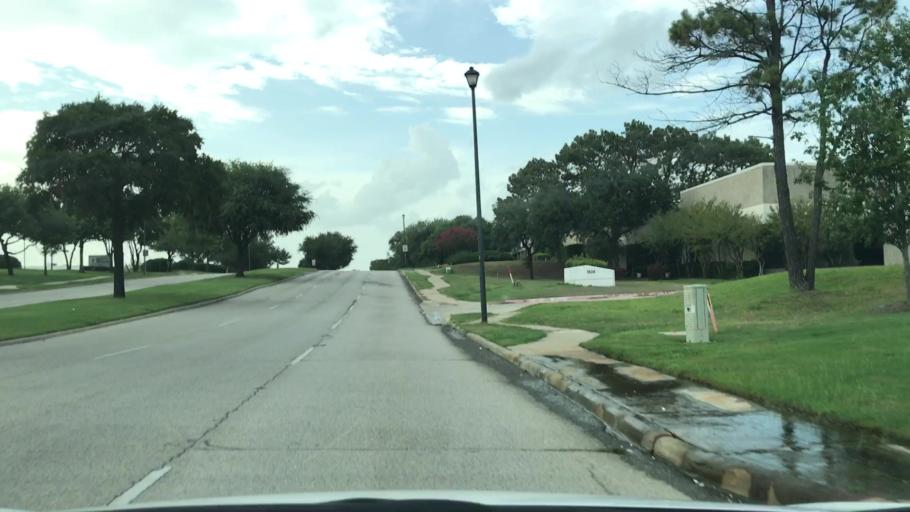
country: US
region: Texas
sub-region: Dallas County
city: Irving
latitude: 32.8779
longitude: -96.9720
